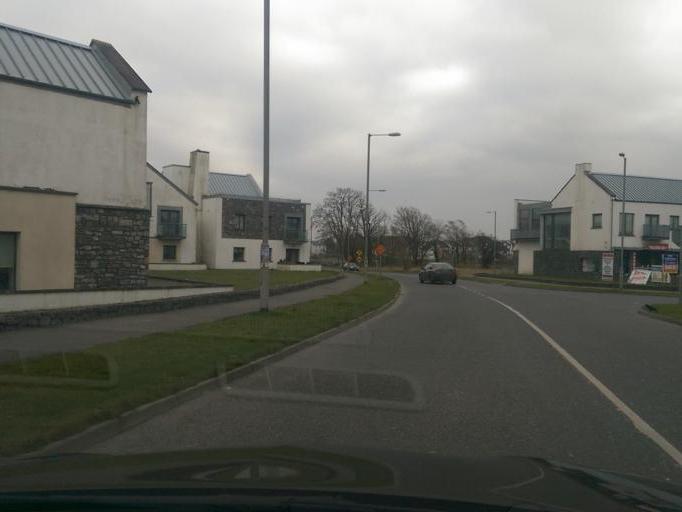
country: IE
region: Connaught
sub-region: County Galway
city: Athenry
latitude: 53.2945
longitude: -8.7490
